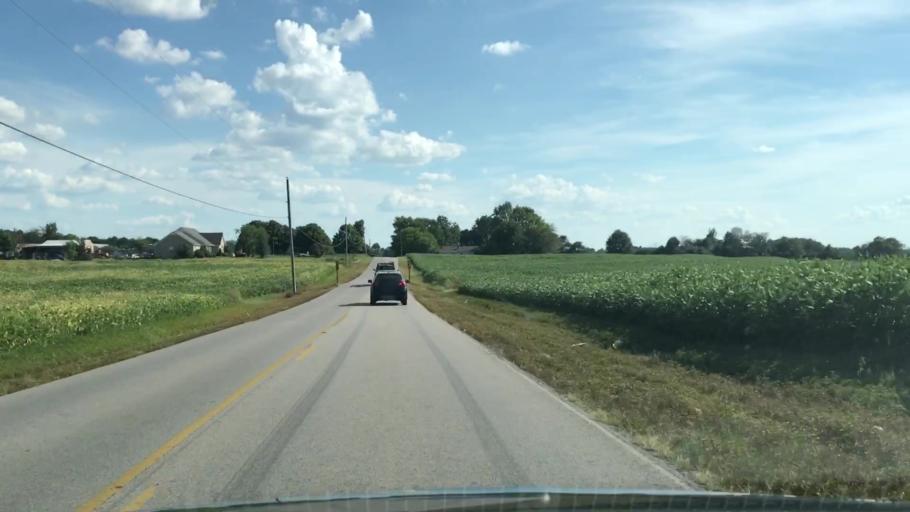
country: US
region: Alabama
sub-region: Madison County
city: Harvest
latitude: 34.8708
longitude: -86.7489
